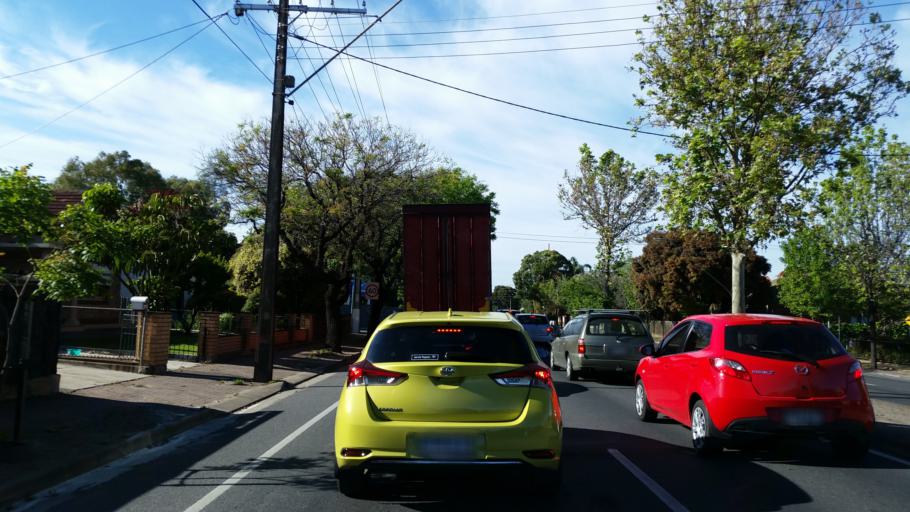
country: AU
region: South Australia
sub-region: Norwood Payneham St Peters
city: Trinity Gardens
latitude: -34.9070
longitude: 138.6400
